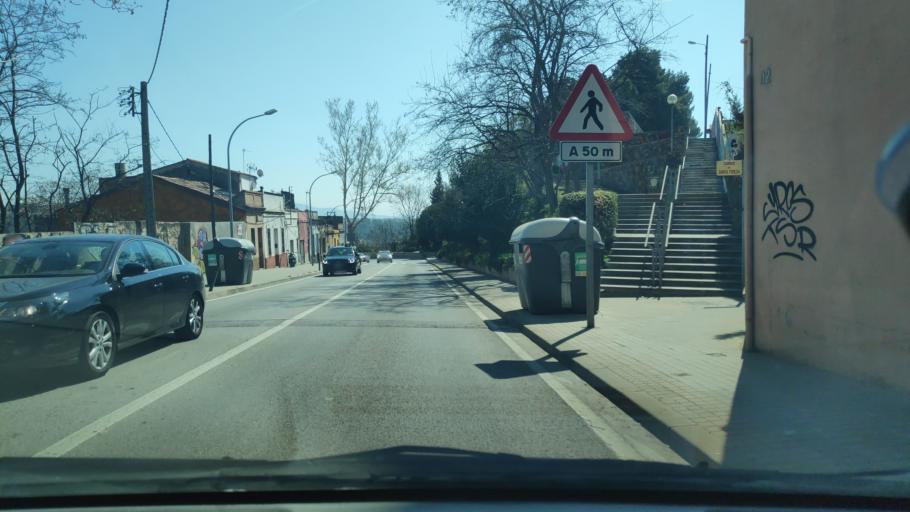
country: ES
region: Catalonia
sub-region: Provincia de Barcelona
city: Sabadell
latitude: 41.5538
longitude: 2.1147
